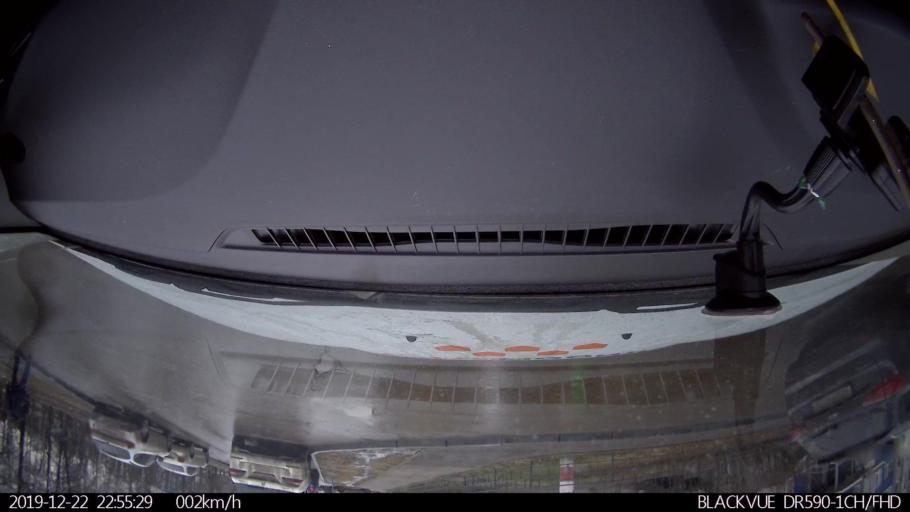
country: RU
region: Nizjnij Novgorod
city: Gorbatovka
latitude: 56.2425
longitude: 43.8457
